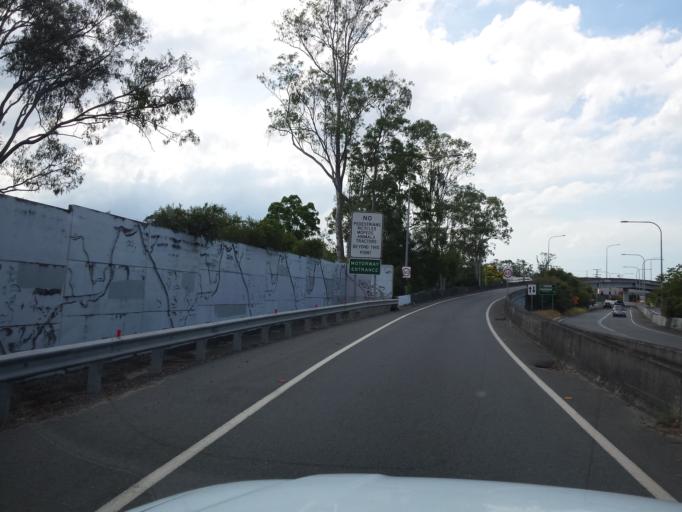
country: AU
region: Queensland
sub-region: Gold Coast
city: Nerang
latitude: -28.0031
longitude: 153.3395
